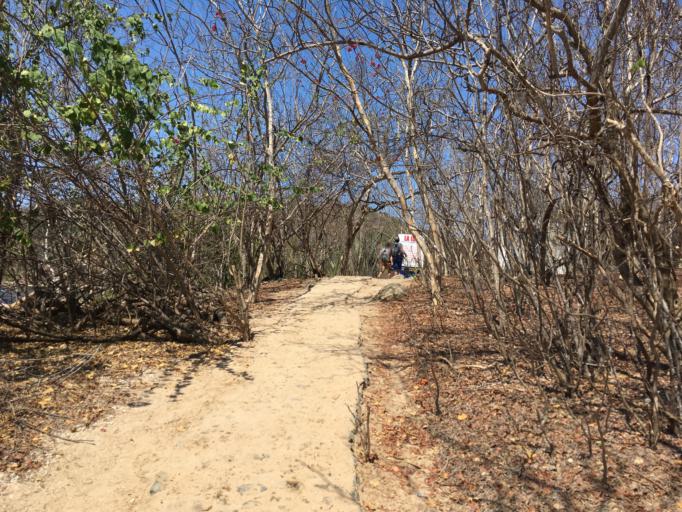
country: MX
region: Guerrero
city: Ixtapa
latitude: 17.6771
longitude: -101.6546
